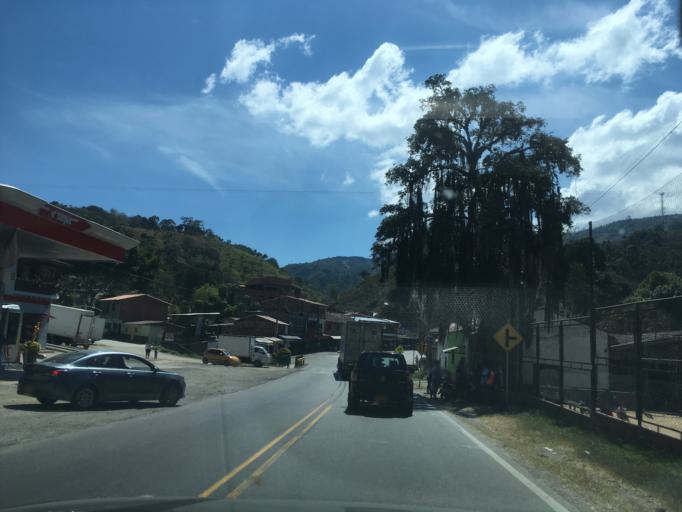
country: CO
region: Santander
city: Aratoca
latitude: 6.6995
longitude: -73.0145
